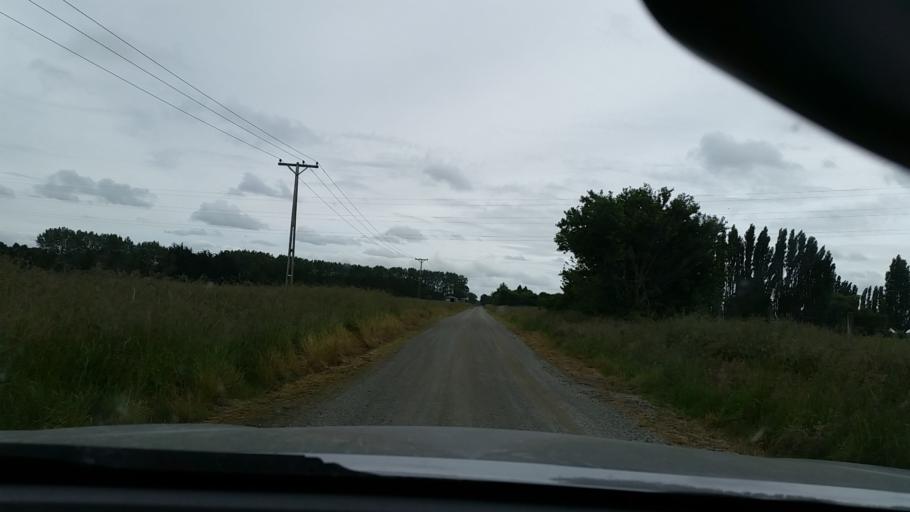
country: NZ
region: Southland
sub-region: Southland District
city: Winton
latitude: -46.1431
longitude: 168.2915
